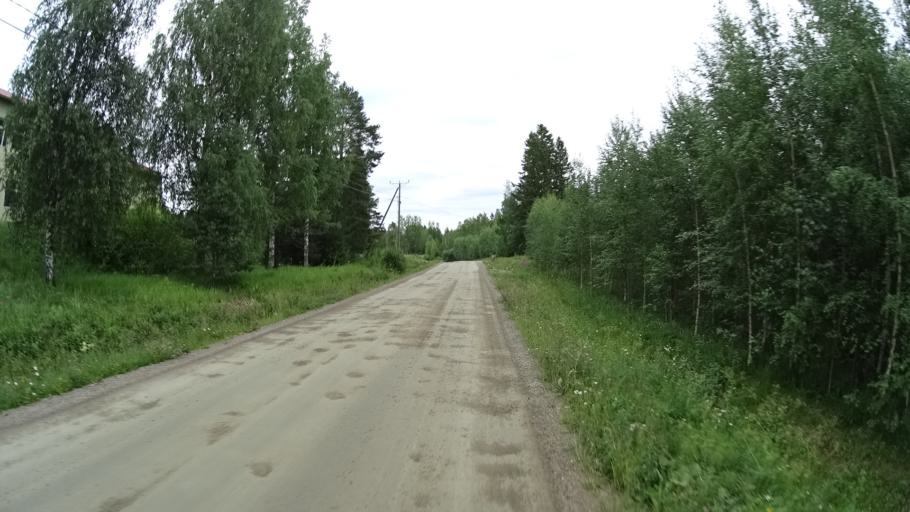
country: FI
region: Satakunta
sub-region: Pohjois-Satakunta
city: Jaemijaervi
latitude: 61.7708
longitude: 22.8541
